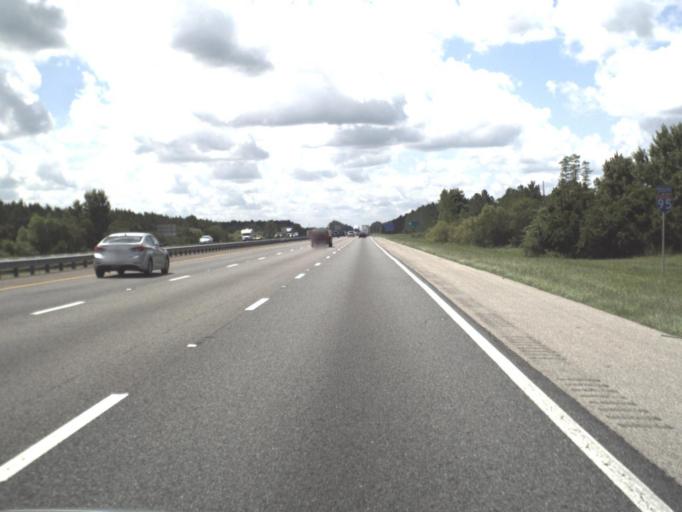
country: US
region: Florida
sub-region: Saint Johns County
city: Saint Augustine Shores
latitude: 29.7407
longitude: -81.3438
